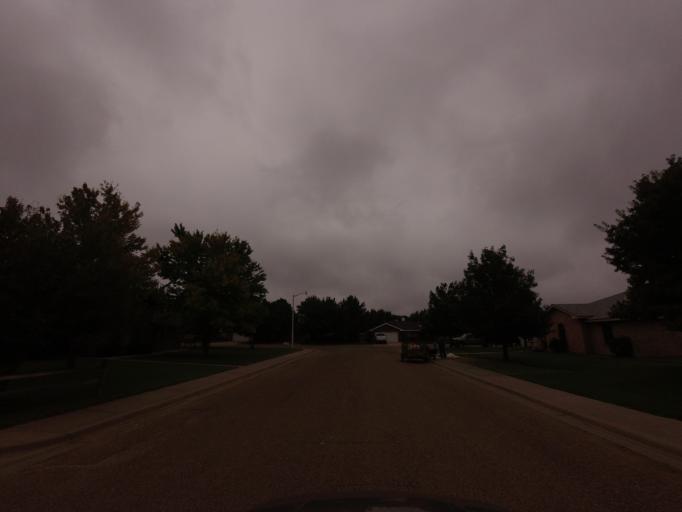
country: US
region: New Mexico
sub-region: Curry County
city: Clovis
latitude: 34.4329
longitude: -103.1804
